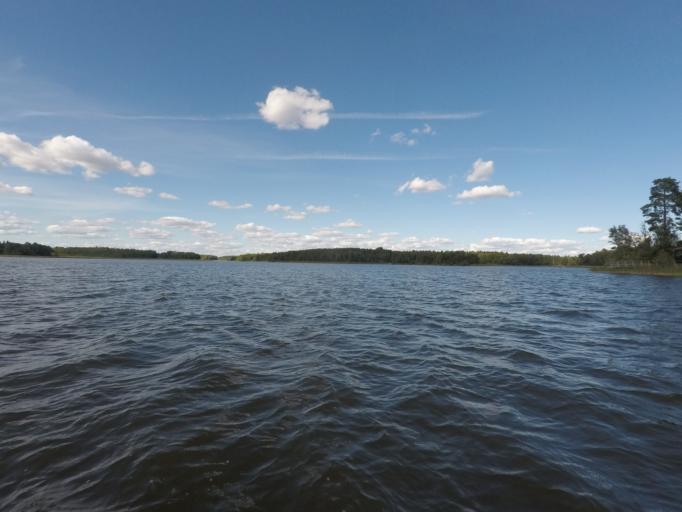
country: SE
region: Soedermanland
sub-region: Eskilstuna Kommun
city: Torshalla
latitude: 59.4759
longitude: 16.4483
